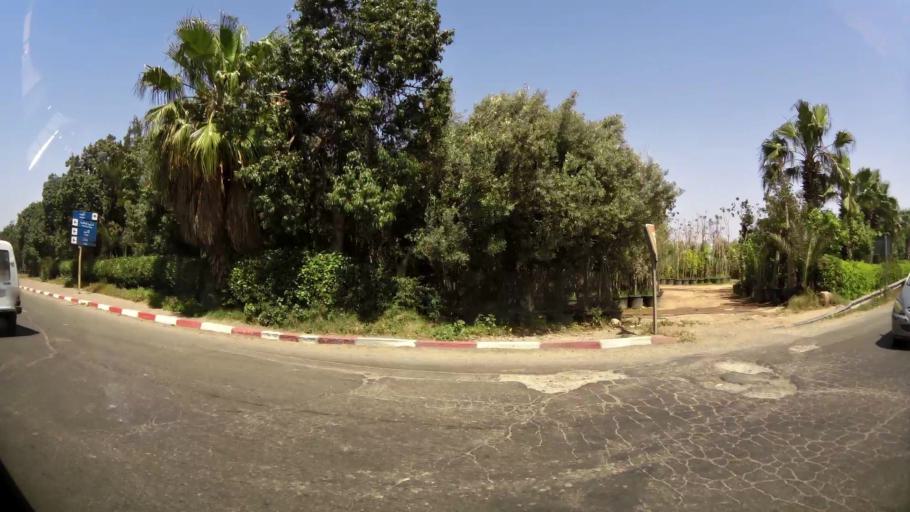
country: MA
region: Souss-Massa-Draa
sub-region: Inezgane-Ait Mellou
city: Inezgane
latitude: 30.3521
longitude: -9.5056
